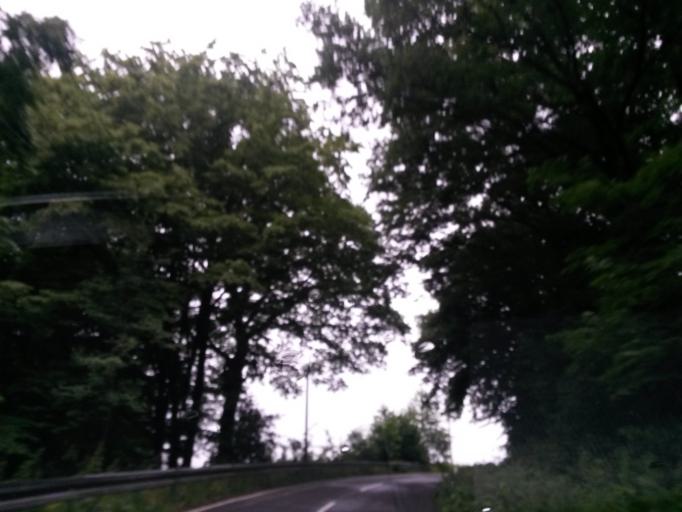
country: DE
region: North Rhine-Westphalia
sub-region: Regierungsbezirk Koln
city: Much
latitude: 50.9474
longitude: 7.3657
